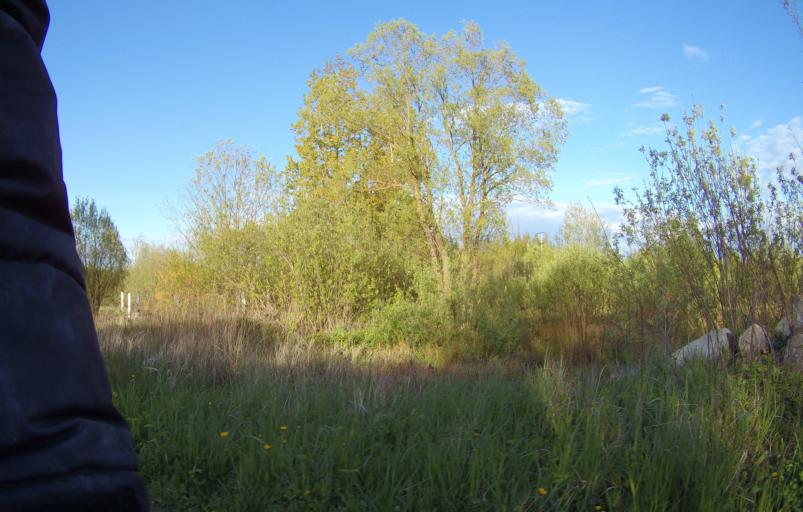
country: RU
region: Moskovskaya
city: Ramenskoye
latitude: 55.5905
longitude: 38.2691
